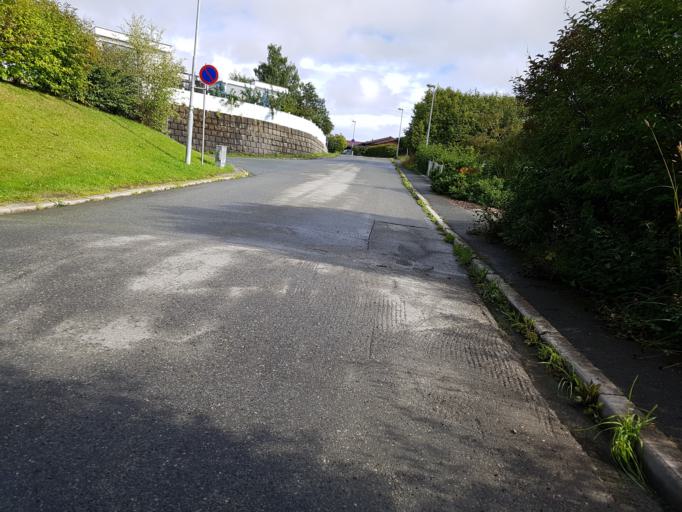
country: NO
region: Sor-Trondelag
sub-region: Trondheim
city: Trondheim
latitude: 63.4103
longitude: 10.4260
